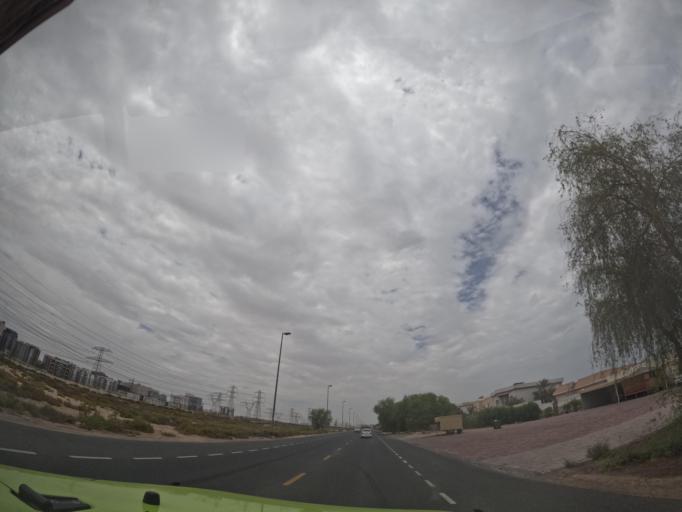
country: AE
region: Ash Shariqah
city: Sharjah
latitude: 25.1965
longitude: 55.3907
